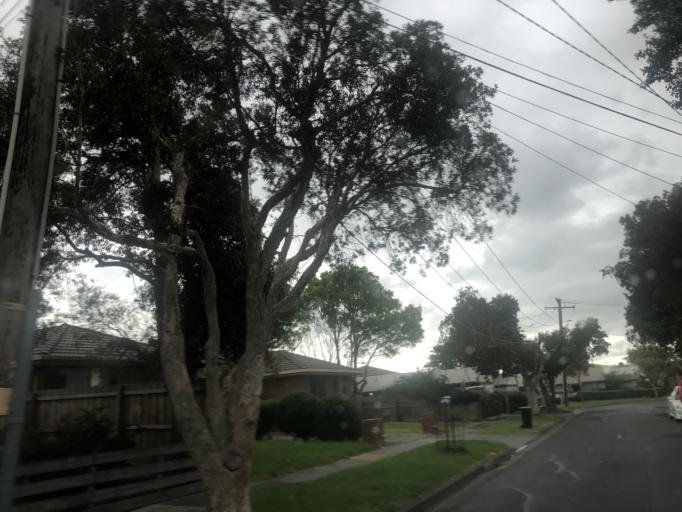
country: AU
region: Victoria
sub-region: Greater Dandenong
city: Dandenong
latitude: -37.9841
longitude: 145.2068
